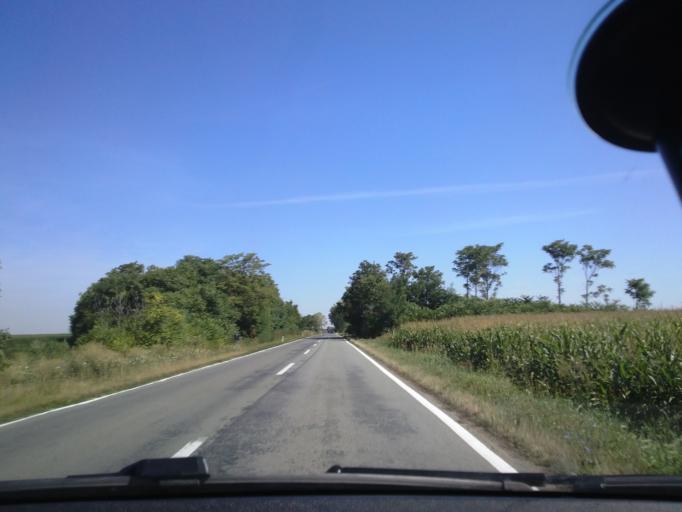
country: RS
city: Doroslovo
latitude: 45.6431
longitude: 19.1990
